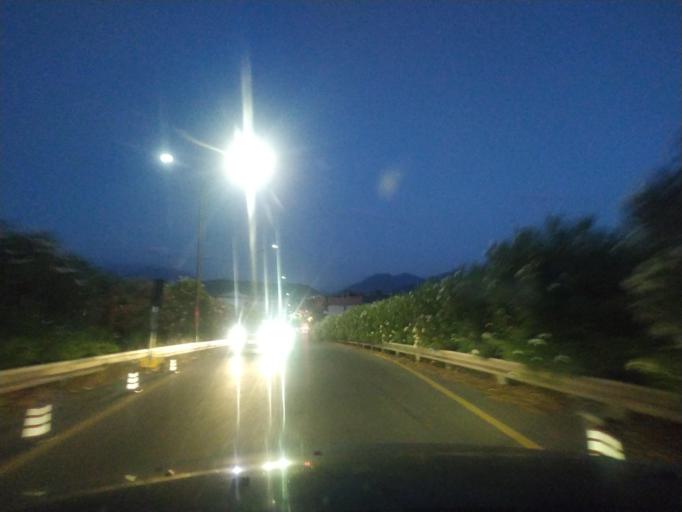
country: IT
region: Sicily
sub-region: Messina
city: Terme
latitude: 38.1413
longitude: 15.1608
